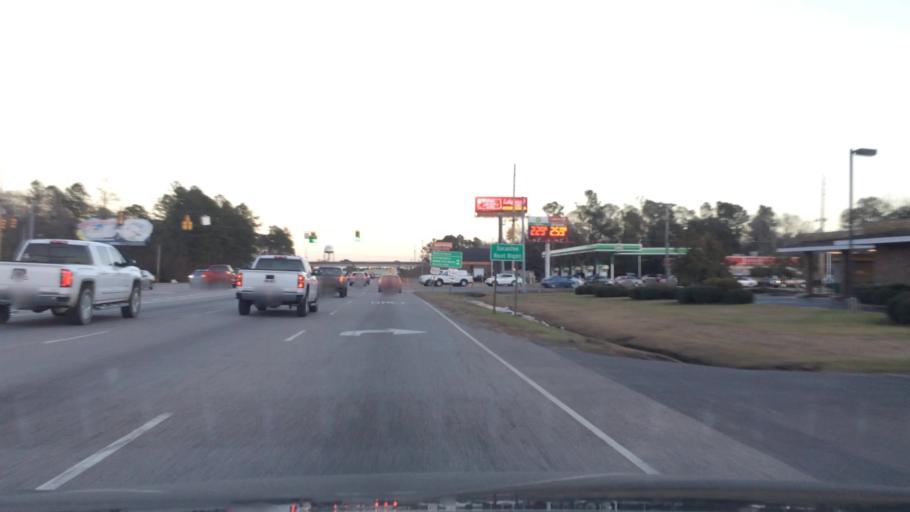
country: US
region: South Carolina
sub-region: Horry County
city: Red Hill
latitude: 33.8075
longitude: -79.0195
